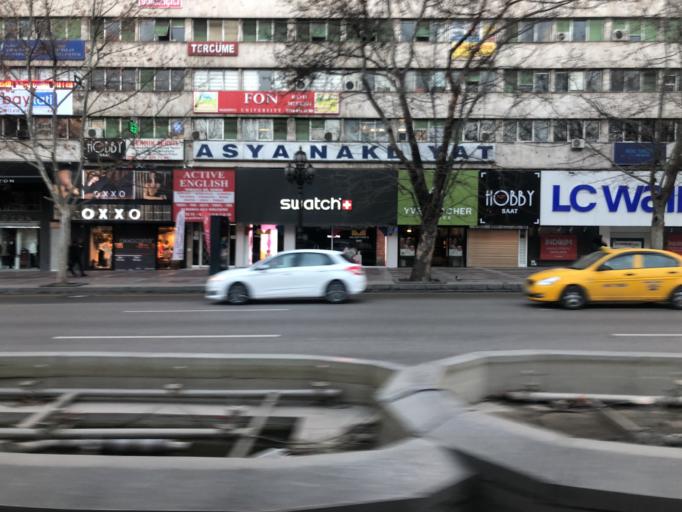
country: TR
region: Ankara
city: Ankara
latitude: 39.9172
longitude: 32.8541
